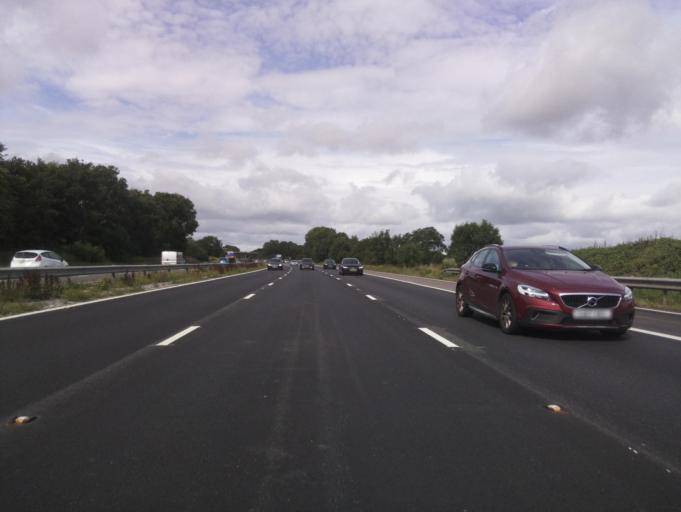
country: GB
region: England
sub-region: Wiltshire
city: Nettleton
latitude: 51.5187
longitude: -2.2662
